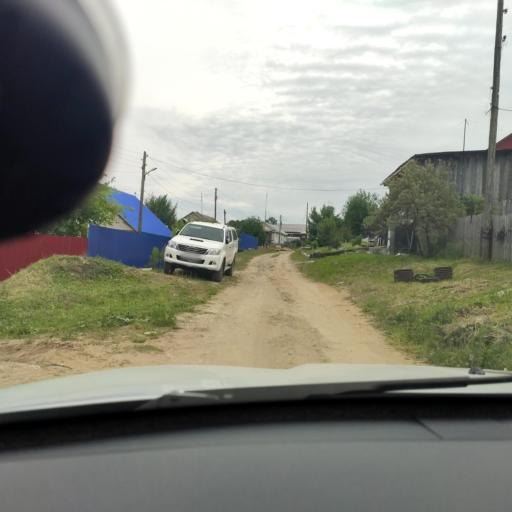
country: RU
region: Perm
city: Polazna
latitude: 58.3026
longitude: 56.4001
